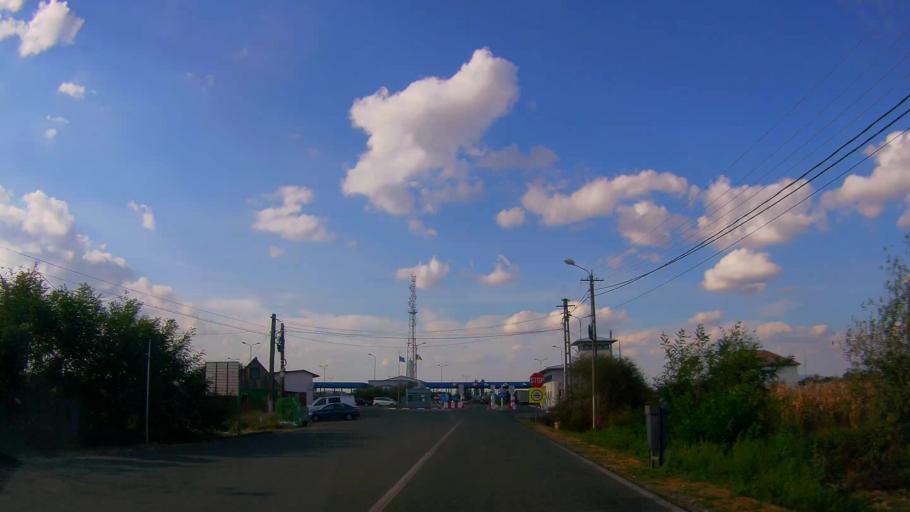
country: RO
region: Satu Mare
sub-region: Comuna Porumbesti
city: Porumbesti
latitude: 47.9908
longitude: 23.0041
